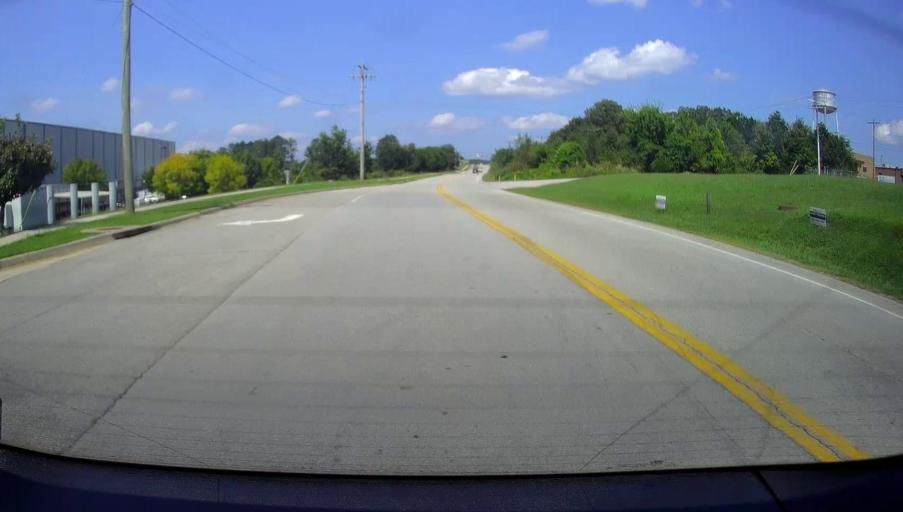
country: US
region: Tennessee
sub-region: Hamilton County
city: Harrison
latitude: 35.0739
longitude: -85.1558
